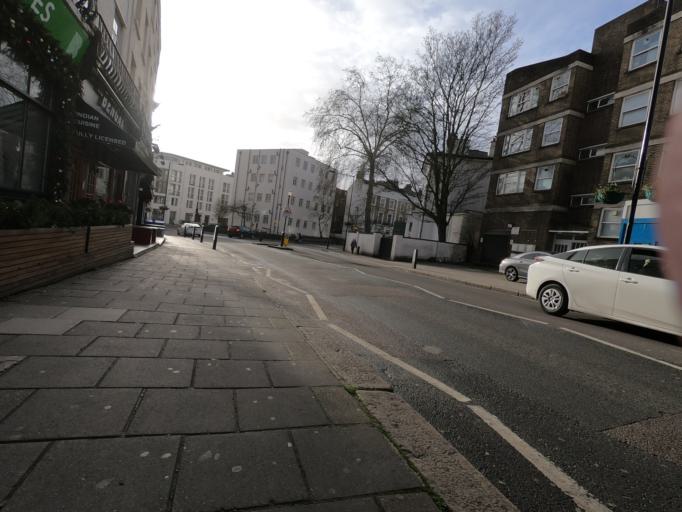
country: GB
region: England
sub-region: Greater London
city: Bayswater
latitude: 51.5185
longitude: -0.1890
